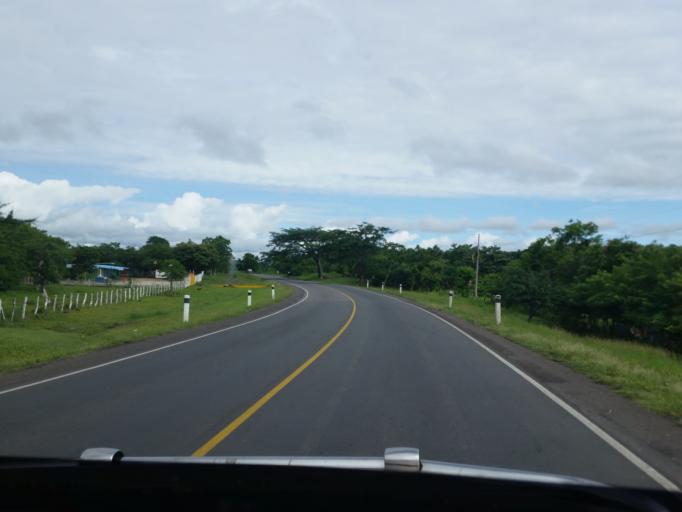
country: NI
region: Matagalpa
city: Ciudad Dario
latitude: 12.5453
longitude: -86.0491
